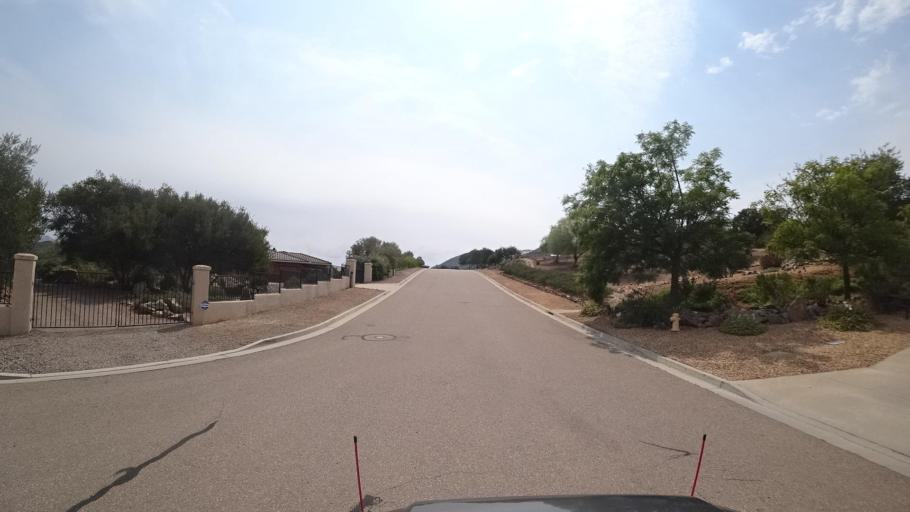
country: US
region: California
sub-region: San Diego County
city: Ramona
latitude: 32.9986
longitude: -116.8898
